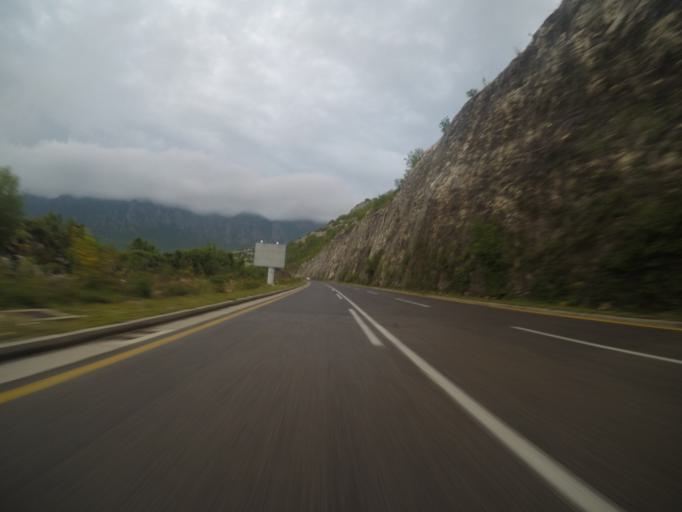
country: ME
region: Bar
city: Sutomore
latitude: 42.2147
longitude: 19.0489
